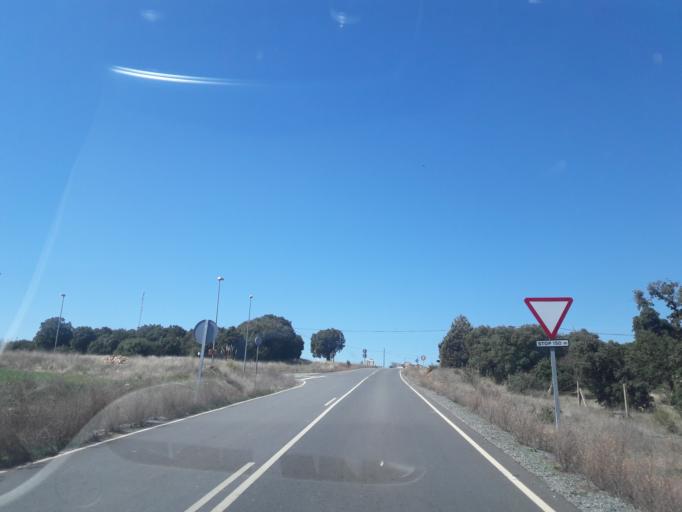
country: ES
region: Castille and Leon
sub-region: Provincia de Salamanca
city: Martinamor
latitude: 40.8103
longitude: -5.6285
